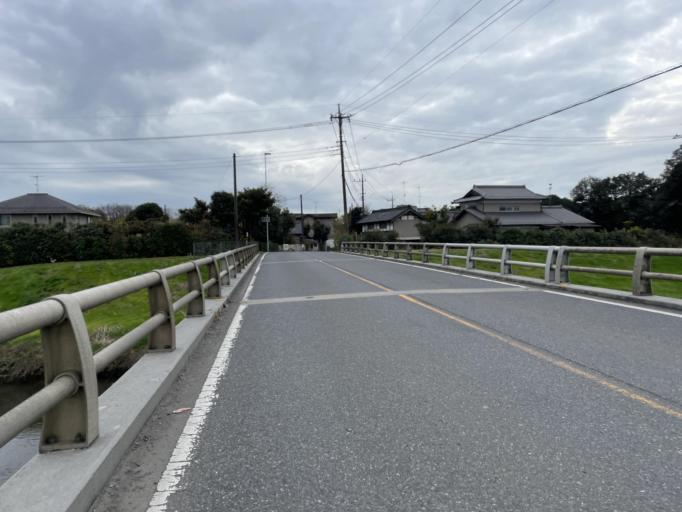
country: JP
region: Saitama
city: Shiraoka
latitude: 36.0325
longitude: 139.6394
